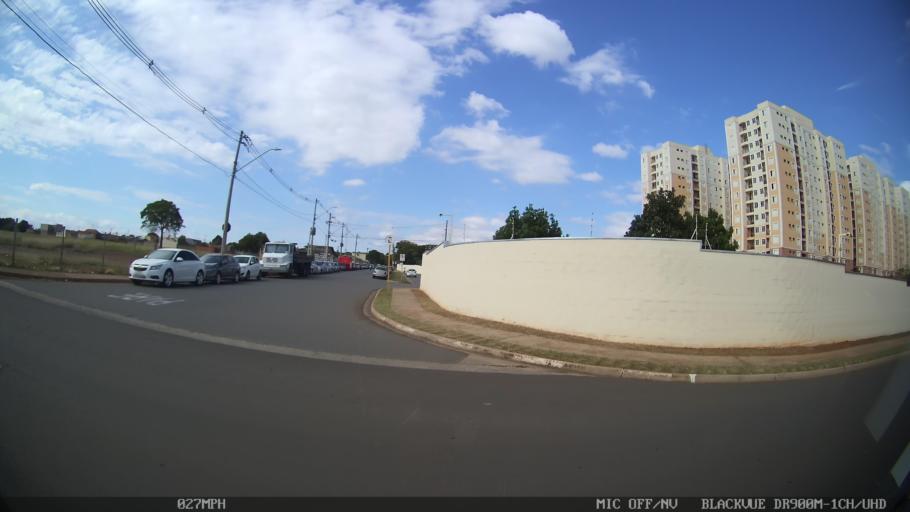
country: BR
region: Sao Paulo
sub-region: Americana
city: Americana
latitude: -22.7218
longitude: -47.3170
